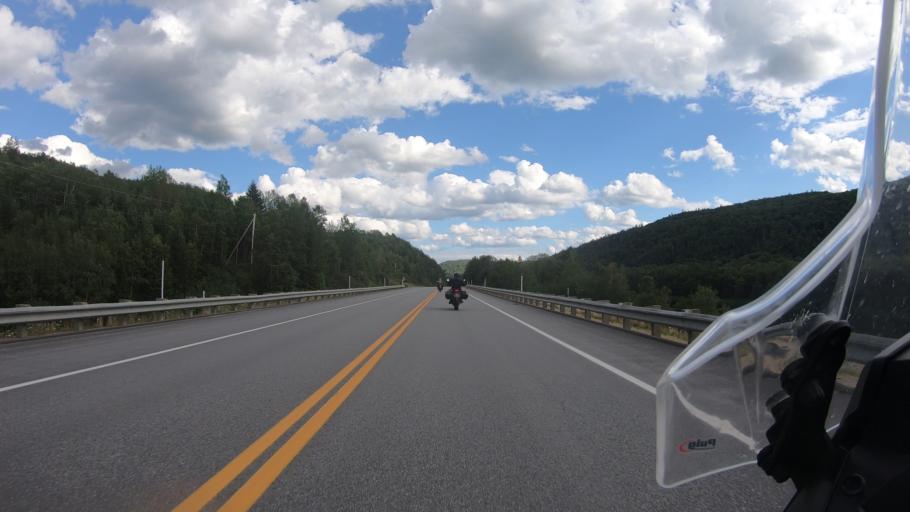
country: CA
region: Quebec
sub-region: Mauricie
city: Saint-Tite
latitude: 47.0051
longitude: -72.9267
